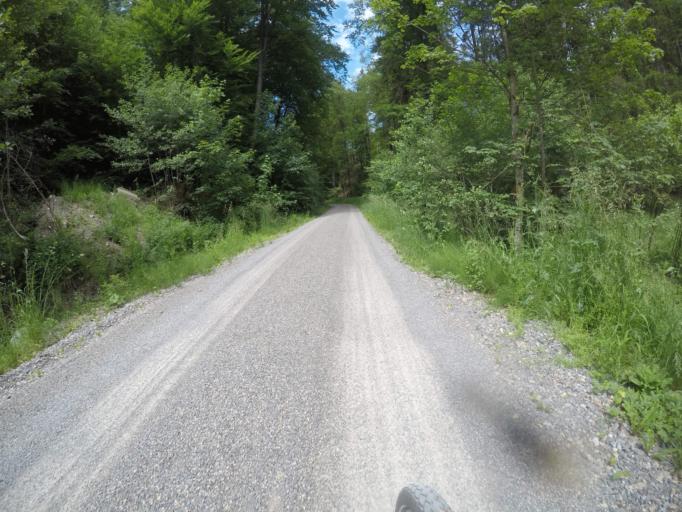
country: DE
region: Baden-Wuerttemberg
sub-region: Regierungsbezirk Stuttgart
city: Hildrizhausen
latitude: 48.6015
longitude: 8.9814
